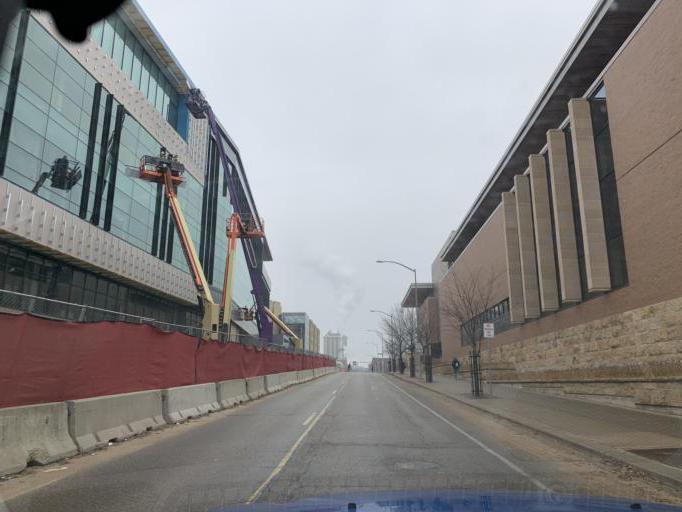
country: US
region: Wisconsin
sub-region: Dane County
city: Madison
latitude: 43.0709
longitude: -89.3978
